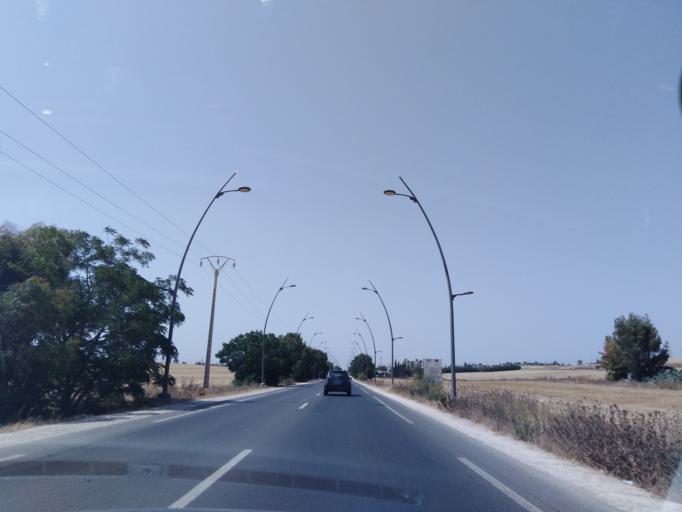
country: MA
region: Chaouia-Ouardigha
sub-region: Settat Province
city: Settat
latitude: 32.9725
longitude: -7.6253
